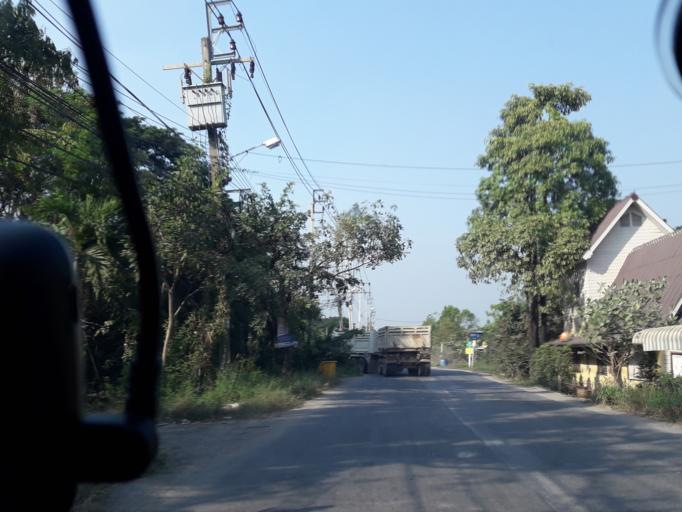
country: TH
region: Pathum Thani
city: Lam Luk Ka
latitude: 13.9127
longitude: 100.7363
